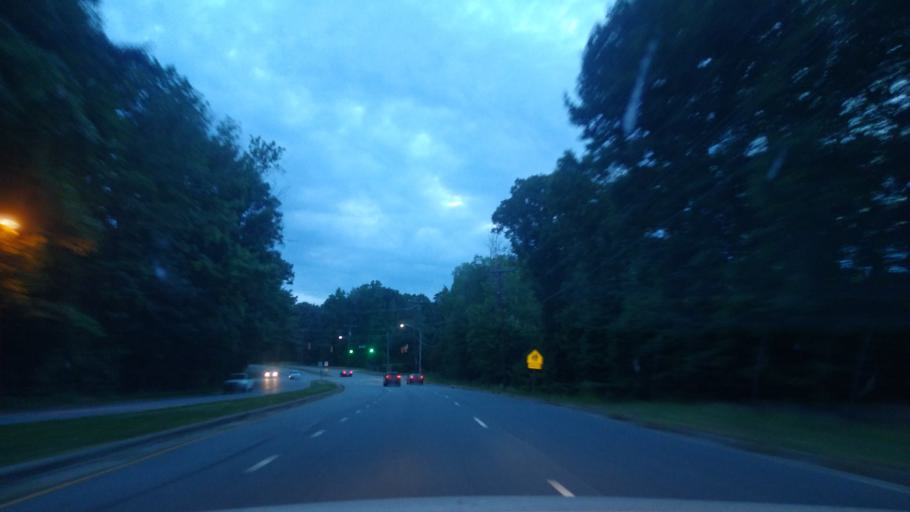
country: US
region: North Carolina
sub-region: Guilford County
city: Greensboro
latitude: 36.1081
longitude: -79.7956
